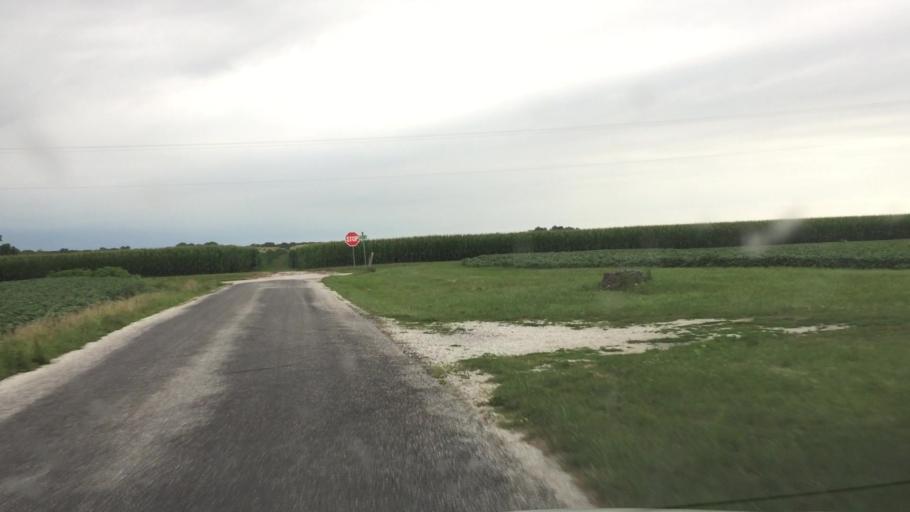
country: US
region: Illinois
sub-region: Adams County
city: Camp Point
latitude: 40.2297
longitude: -90.9690
